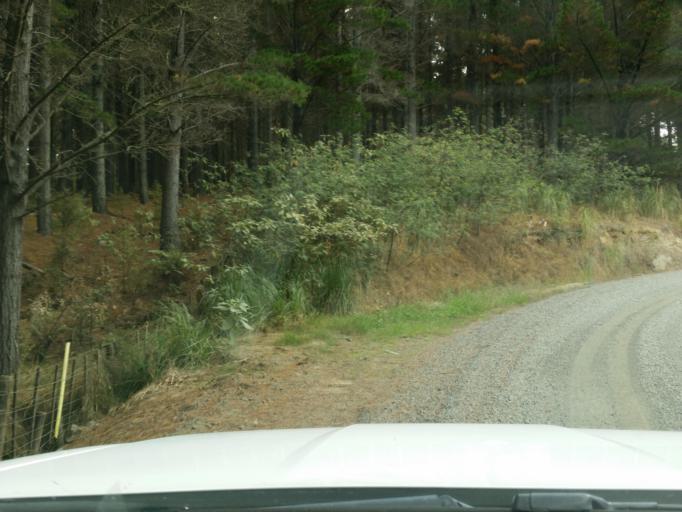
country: NZ
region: Northland
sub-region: Kaipara District
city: Dargaville
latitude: -36.2405
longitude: 174.0896
